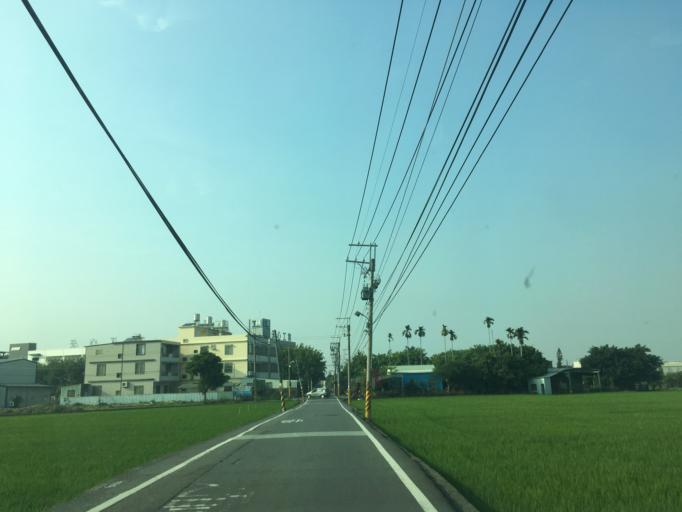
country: TW
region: Taiwan
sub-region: Taichung City
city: Taichung
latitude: 24.0562
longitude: 120.6806
